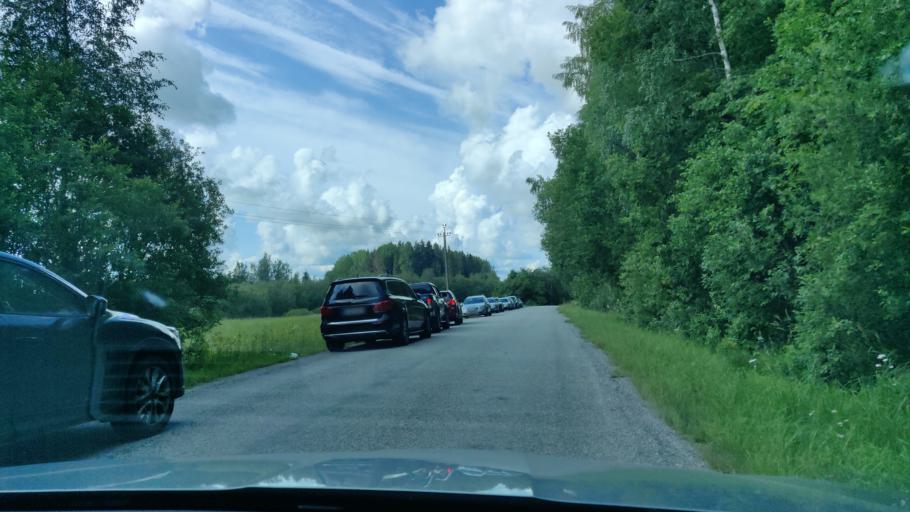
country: EE
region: Tartu
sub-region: Elva linn
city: Elva
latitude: 58.0257
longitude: 26.3420
